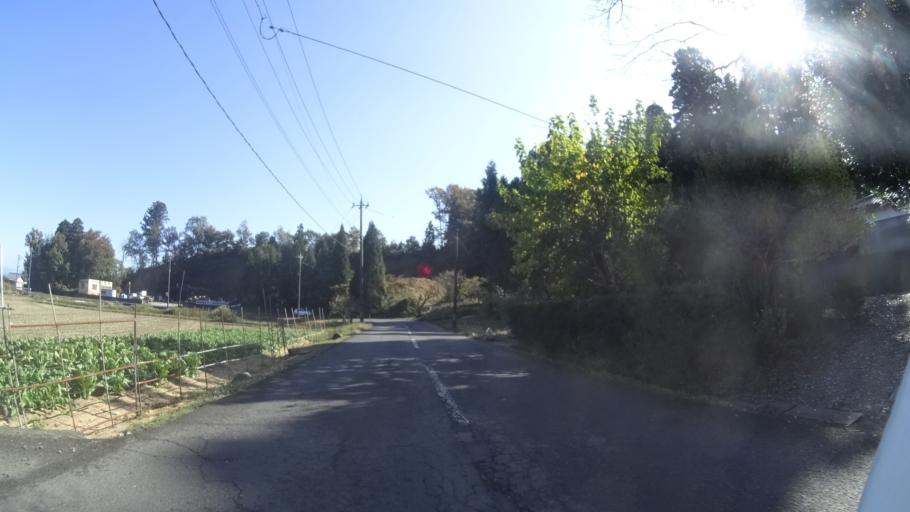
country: JP
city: Asahi
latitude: 35.9625
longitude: 136.1365
